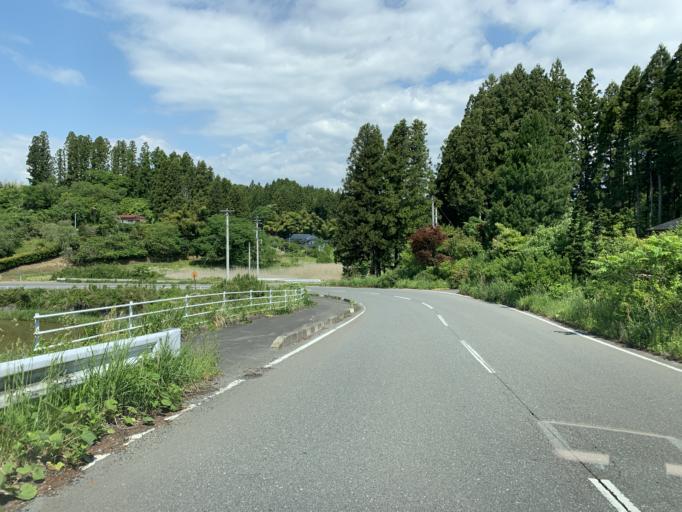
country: JP
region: Miyagi
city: Furukawa
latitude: 38.7034
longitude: 140.9302
